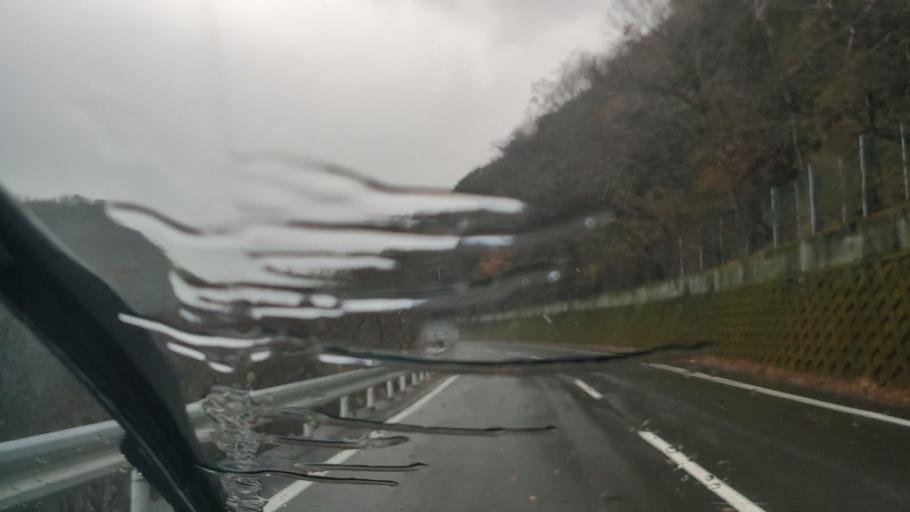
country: JP
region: Tokushima
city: Kamojimacho-jogejima
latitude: 34.1458
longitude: 134.3545
